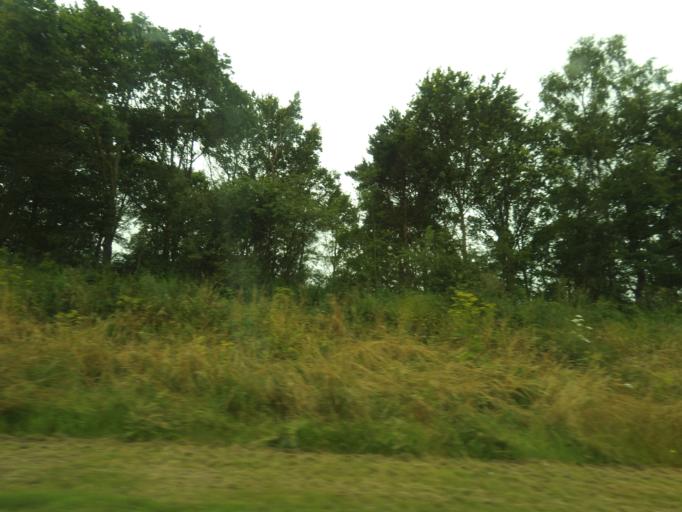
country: DK
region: South Denmark
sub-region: Odense Kommune
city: Stige
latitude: 55.4310
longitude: 10.3765
